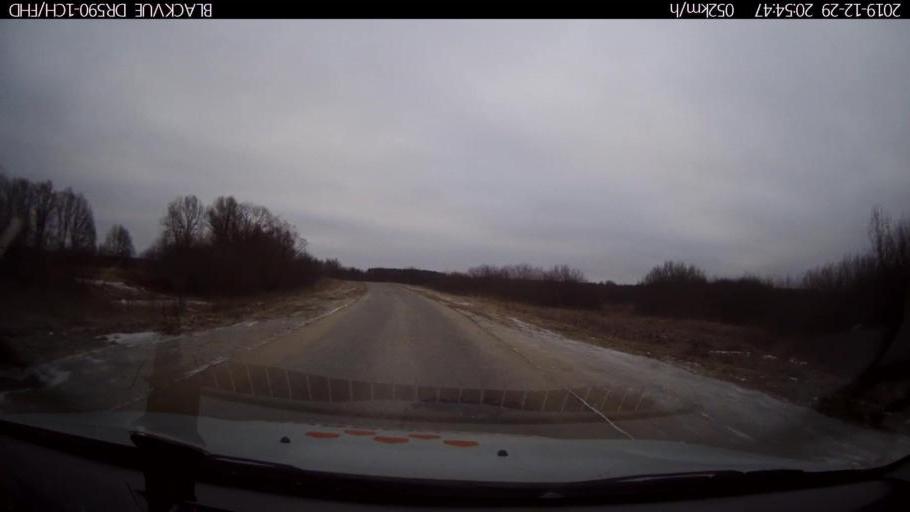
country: RU
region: Nizjnij Novgorod
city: Afonino
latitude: 56.1608
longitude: 43.9911
